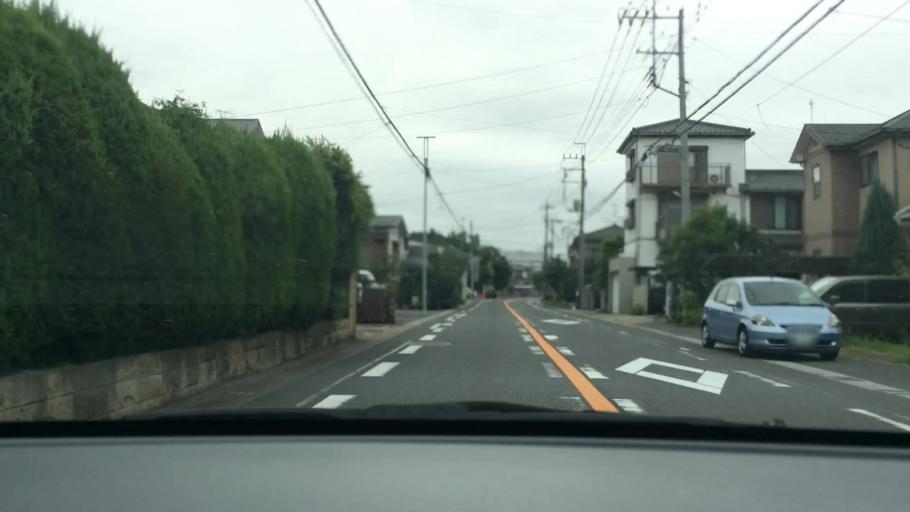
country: JP
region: Chiba
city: Nagareyama
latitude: 35.8631
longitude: 139.9020
